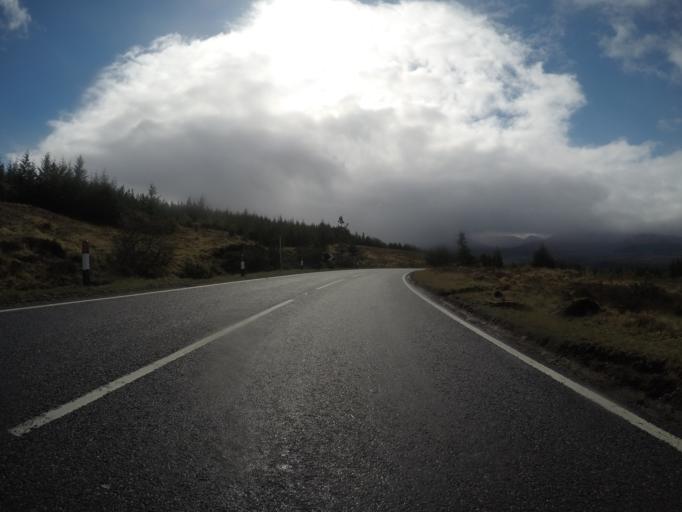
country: GB
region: Scotland
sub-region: Highland
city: Spean Bridge
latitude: 57.0899
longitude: -4.9817
